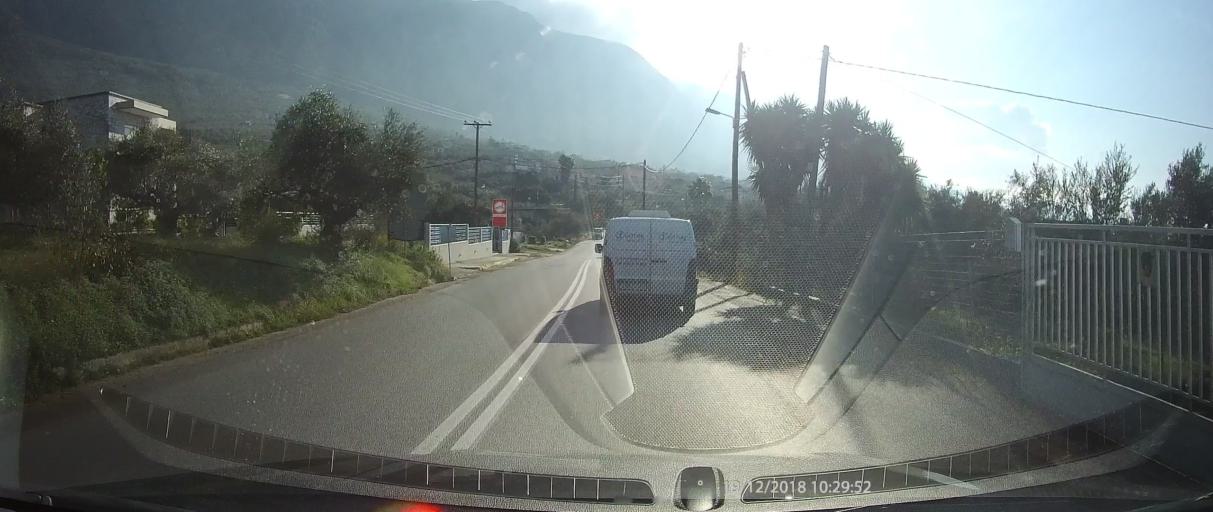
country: GR
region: Peloponnese
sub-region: Nomos Messinias
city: Paralia Vergas
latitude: 37.0198
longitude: 22.1511
